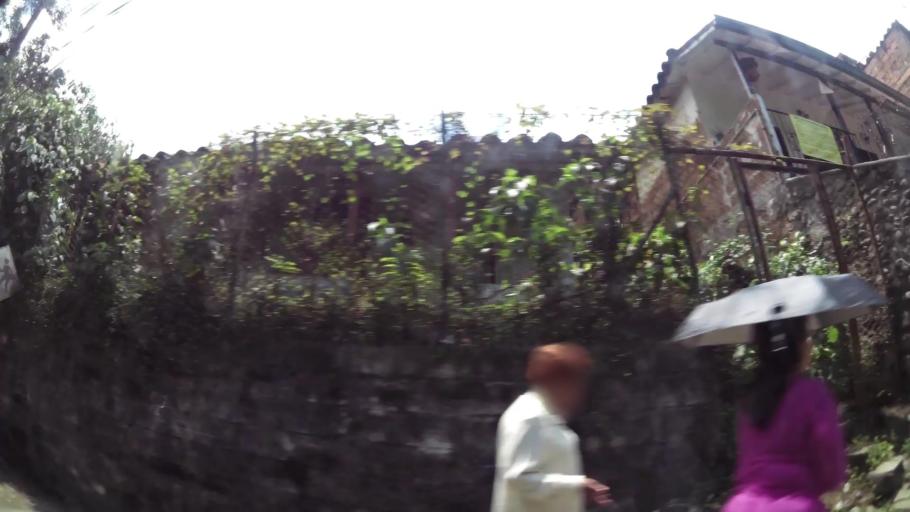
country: CO
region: Antioquia
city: La Estrella
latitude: 6.1645
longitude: -75.6429
